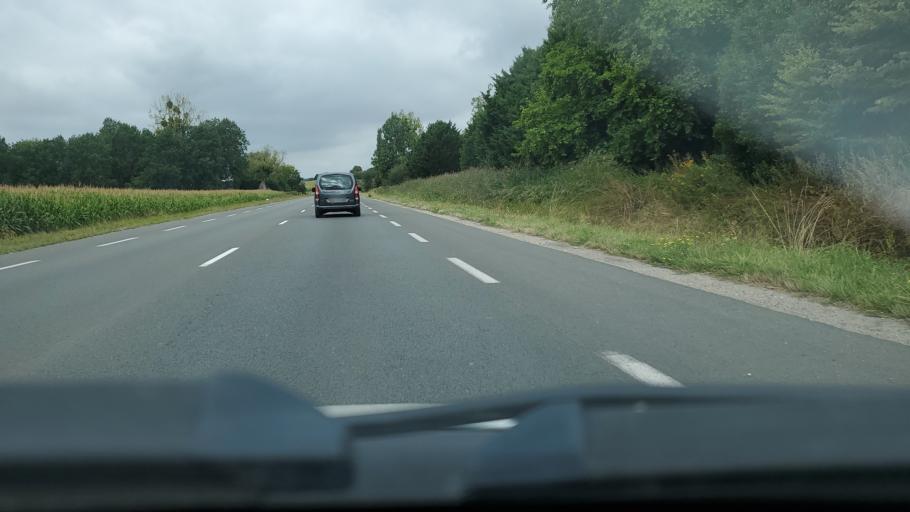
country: FR
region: Ile-de-France
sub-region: Departement de Seine-et-Marne
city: Coulommiers
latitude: 48.8149
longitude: 3.0685
